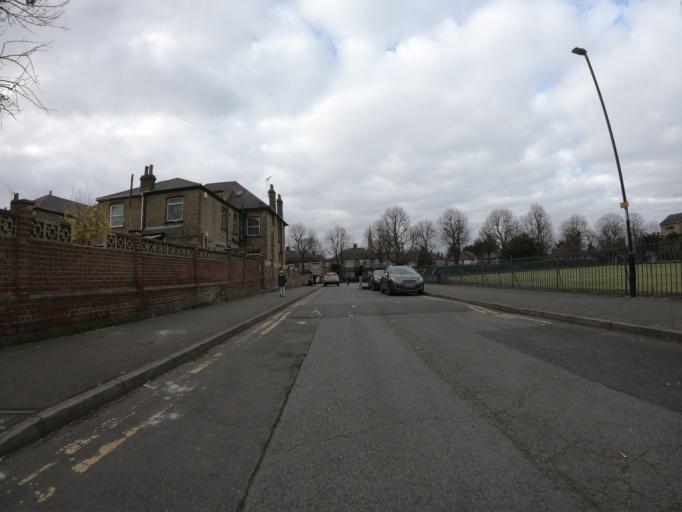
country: GB
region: England
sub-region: Greater London
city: Erith
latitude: 51.4771
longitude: 0.1781
